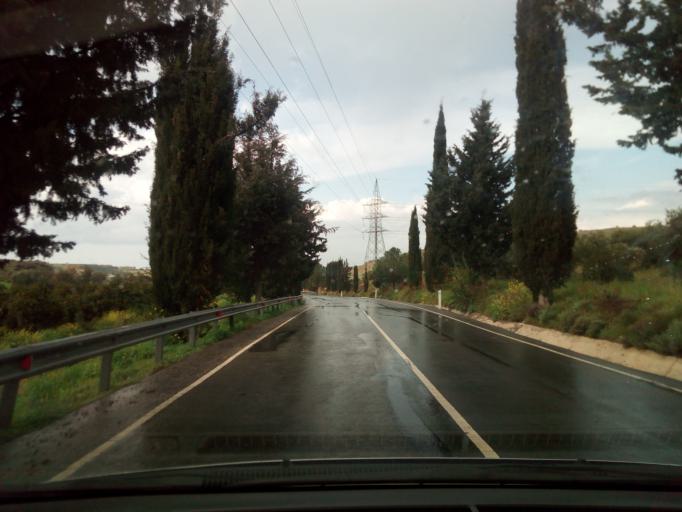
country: CY
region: Pafos
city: Polis
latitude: 35.0234
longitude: 32.4445
